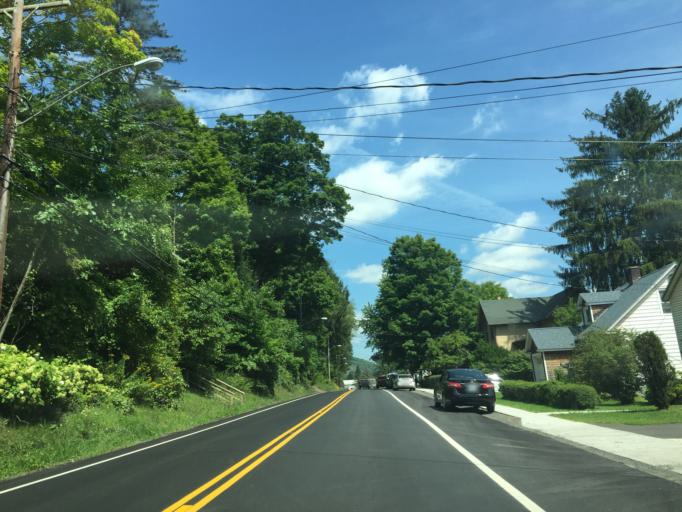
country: US
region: New York
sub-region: Delaware County
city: Delhi
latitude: 42.2824
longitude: -74.9100
